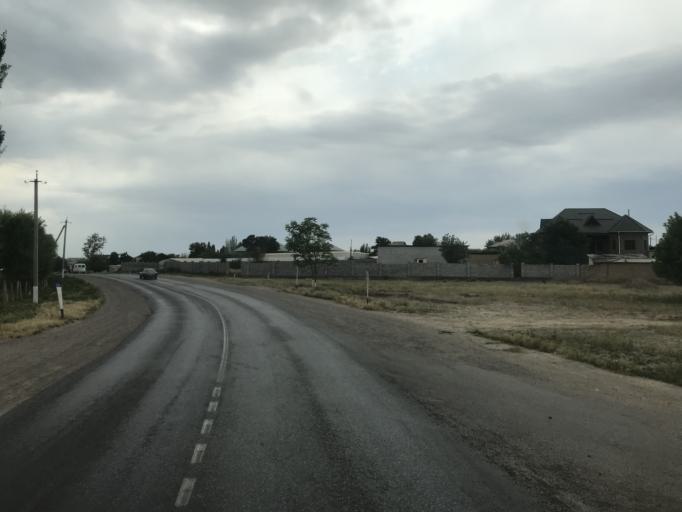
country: KZ
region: Ongtustik Qazaqstan
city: Saryaghash
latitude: 41.3727
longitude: 68.9984
